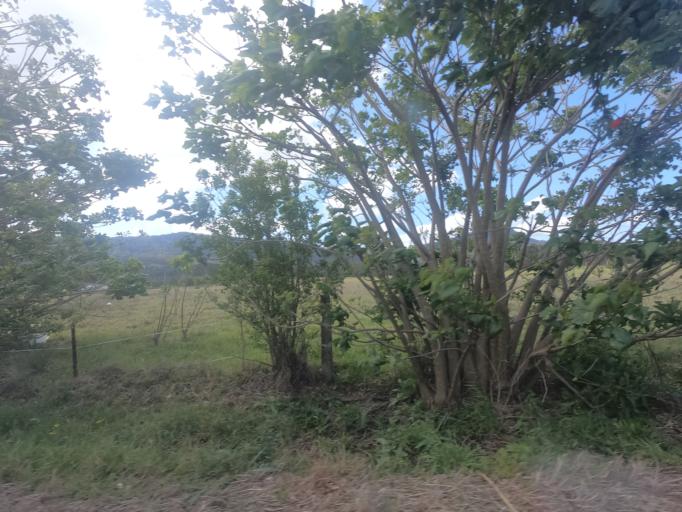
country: AU
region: New South Wales
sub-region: Wollongong
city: Dapto
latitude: -34.4717
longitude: 150.7809
